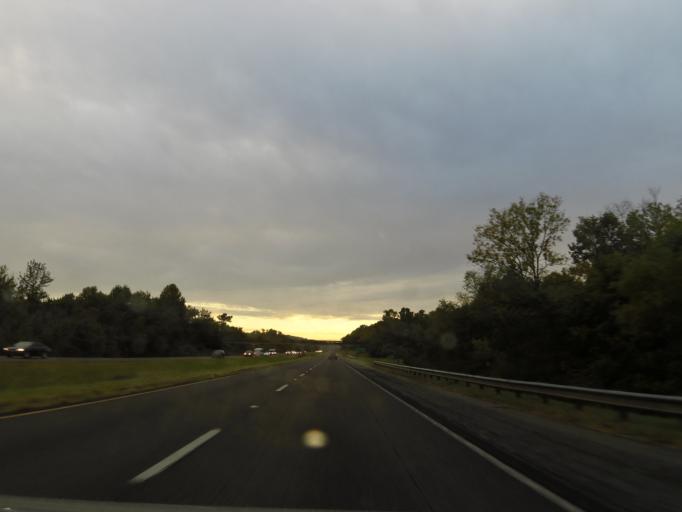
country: US
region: Alabama
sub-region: Jefferson County
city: Argo
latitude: 33.6823
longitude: -86.5364
